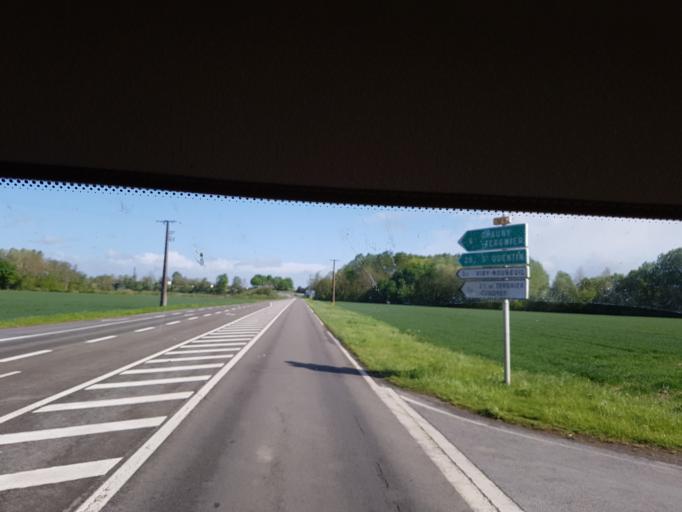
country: FR
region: Picardie
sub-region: Departement de l'Aisne
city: Viry-Noureuil
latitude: 49.6247
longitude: 3.2714
